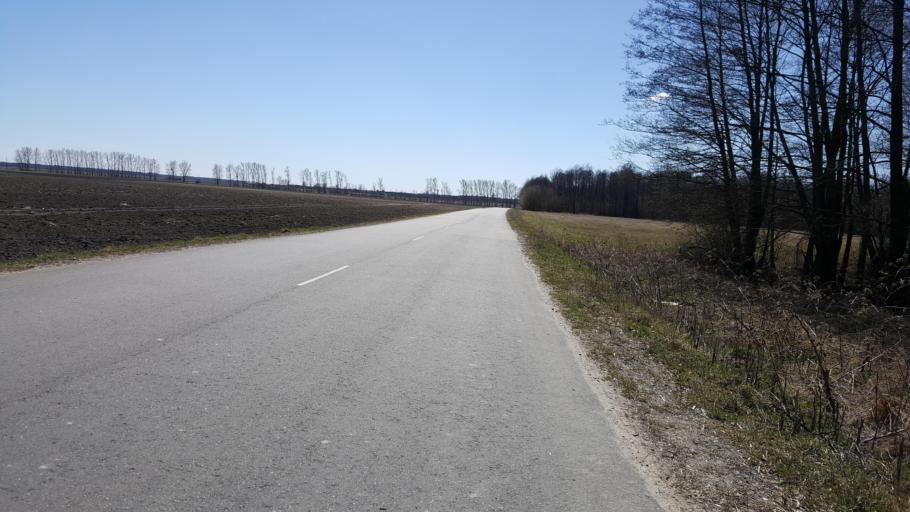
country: BY
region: Brest
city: Kamyanyets
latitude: 52.3051
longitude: 23.8581
